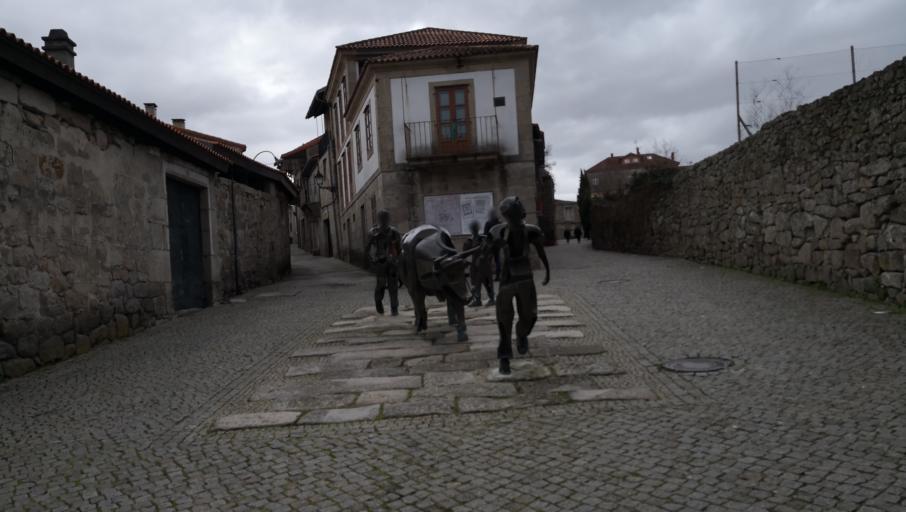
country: ES
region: Galicia
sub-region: Provincia de Ourense
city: Allariz
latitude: 42.1885
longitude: -7.8014
